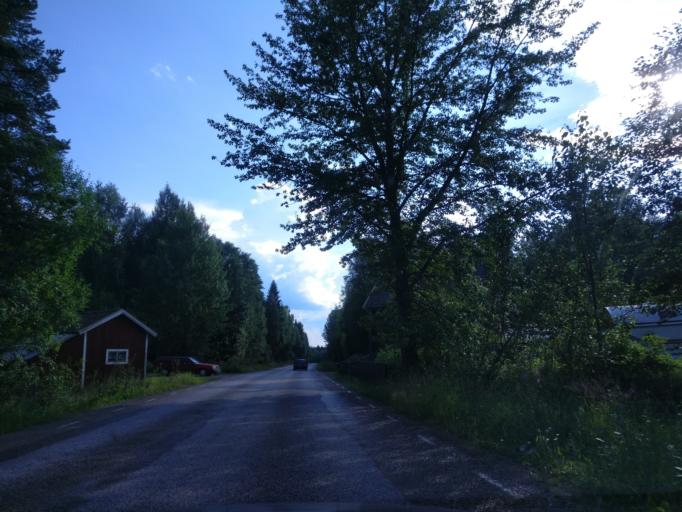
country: SE
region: Dalarna
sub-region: Ludvika Kommun
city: Ludvika
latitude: 60.2789
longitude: 15.0833
